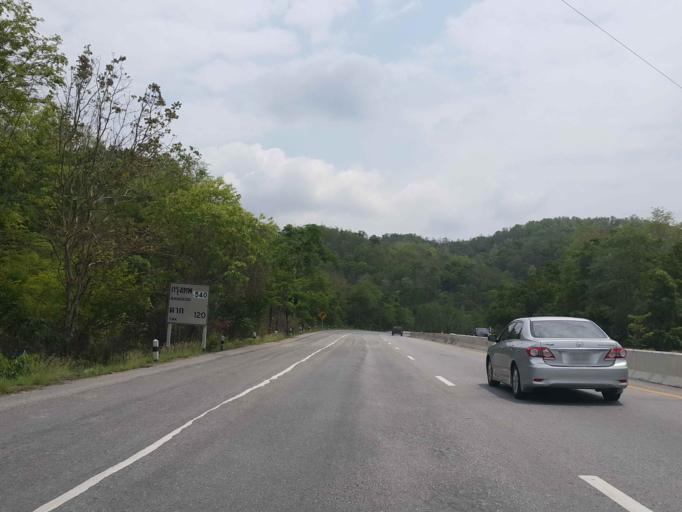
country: TH
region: Lampang
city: Sop Prap
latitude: 17.8334
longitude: 99.2902
